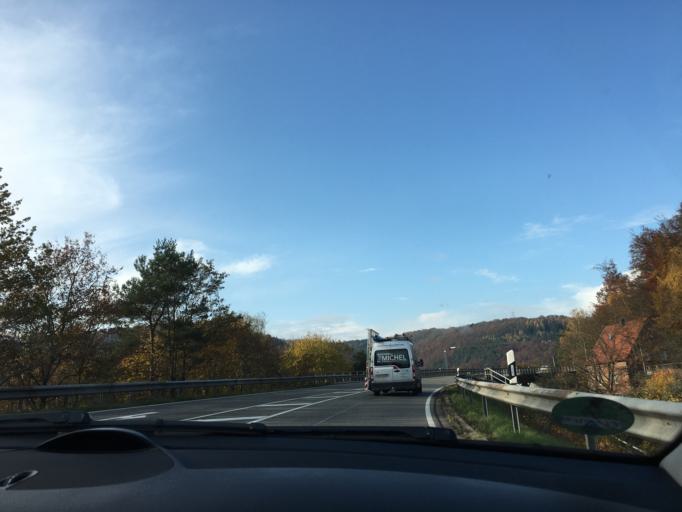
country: DE
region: Rheinland-Pfalz
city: Steinalben
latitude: 49.3133
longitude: 7.6565
